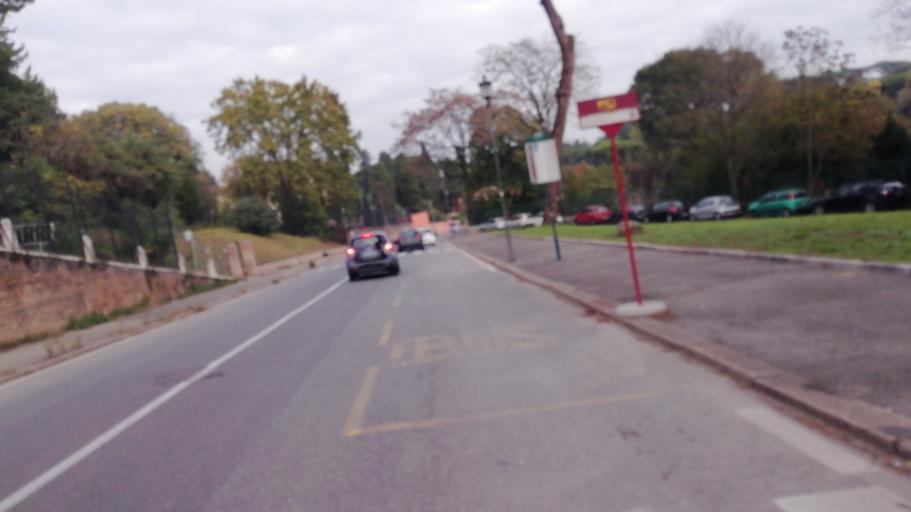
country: IT
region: Latium
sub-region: Citta metropolitana di Roma Capitale
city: Rome
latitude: 41.8806
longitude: 12.4902
